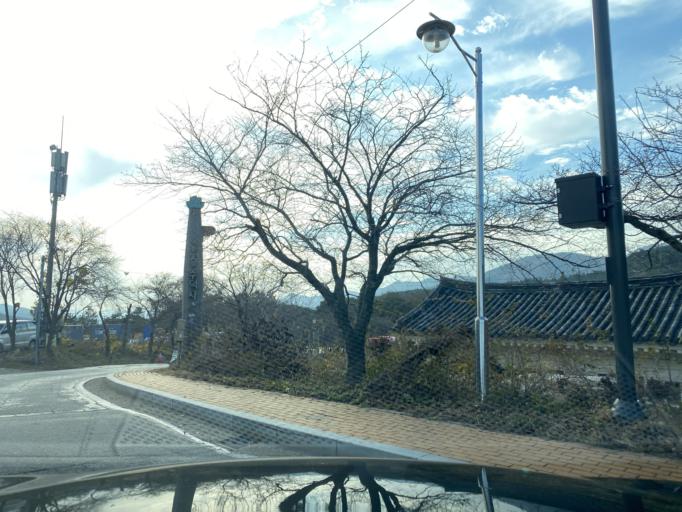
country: KR
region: Chungcheongnam-do
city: Hongsung
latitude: 36.6559
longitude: 126.6211
